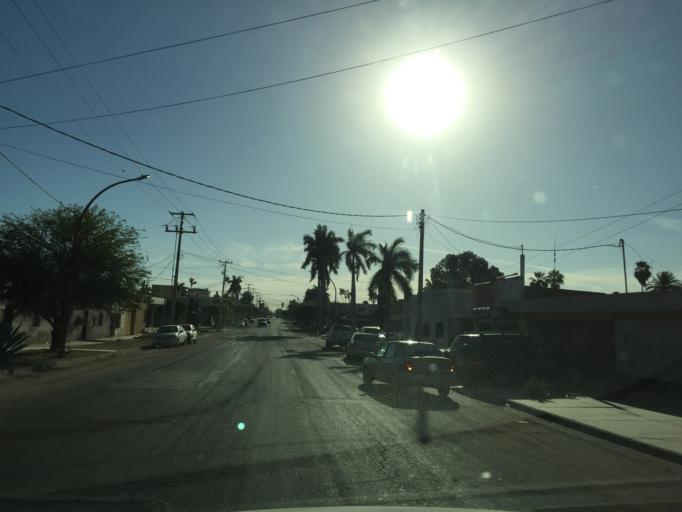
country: MX
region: Sonora
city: Navojoa
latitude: 27.0822
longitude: -109.4491
